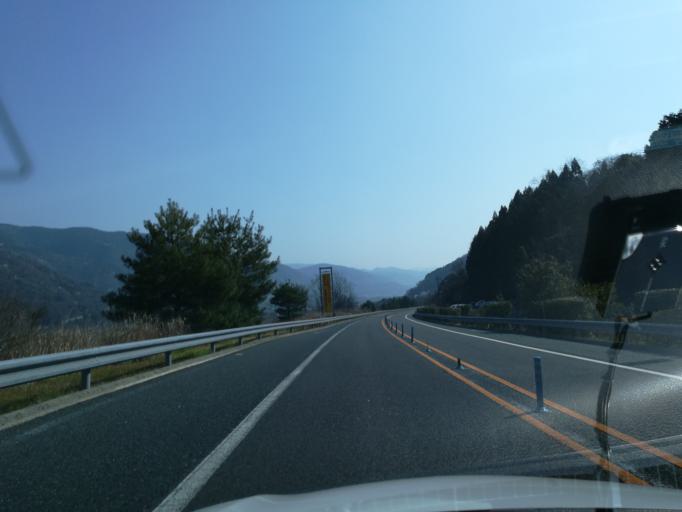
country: JP
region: Tokushima
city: Ikedacho
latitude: 34.0243
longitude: 133.8195
